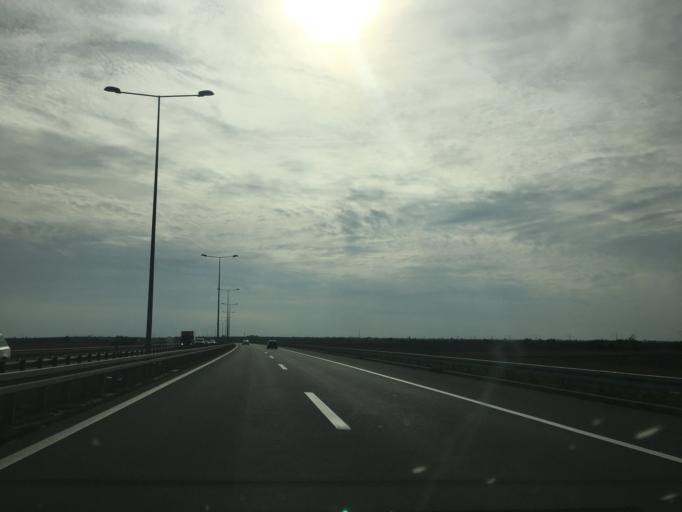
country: RS
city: Dobanovci
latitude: 44.8614
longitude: 20.2511
